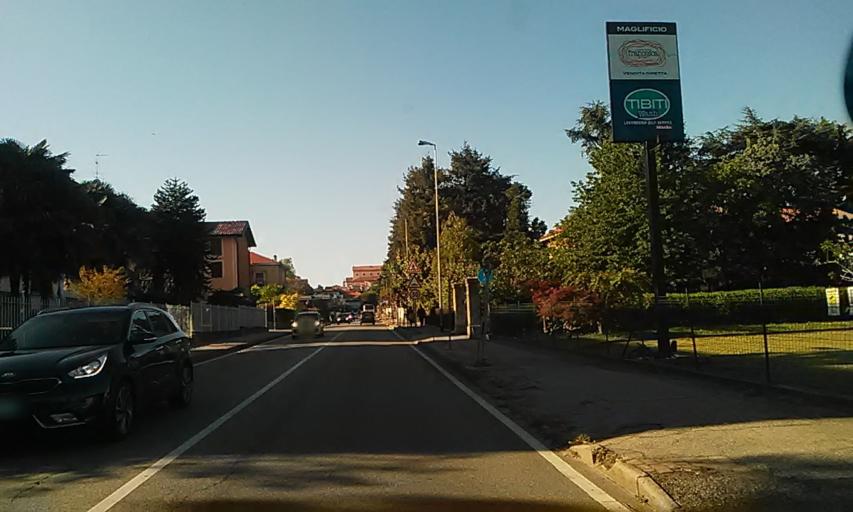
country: IT
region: Piedmont
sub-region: Provincia di Novara
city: Oleggio
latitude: 45.5898
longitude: 8.6387
